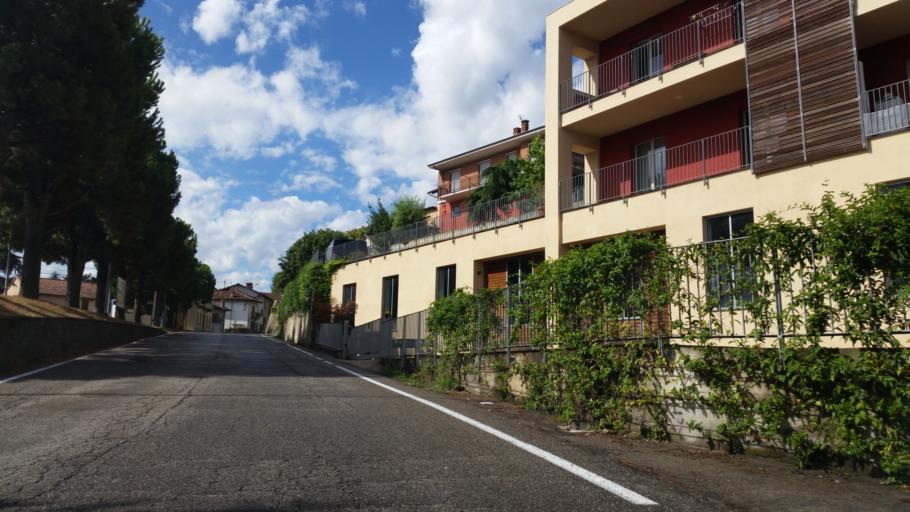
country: IT
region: Piedmont
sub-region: Provincia di Cuneo
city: Castagnito
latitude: 44.7561
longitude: 8.0325
